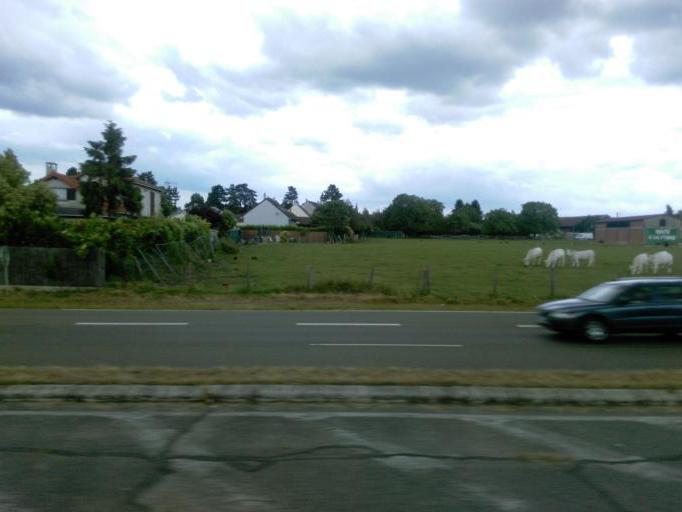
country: FR
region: Ile-de-France
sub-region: Departement du Val-d'Oise
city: Osny
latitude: 49.0861
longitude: 2.0637
